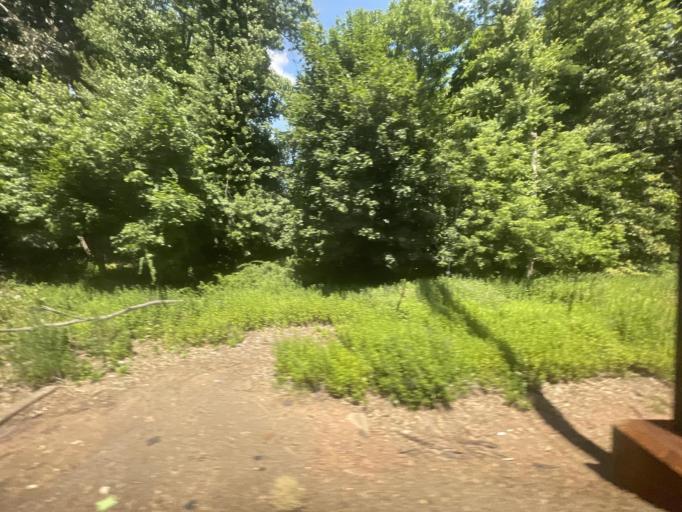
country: US
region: New Jersey
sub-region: Middlesex County
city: Metuchen
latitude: 40.5437
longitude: -74.3527
